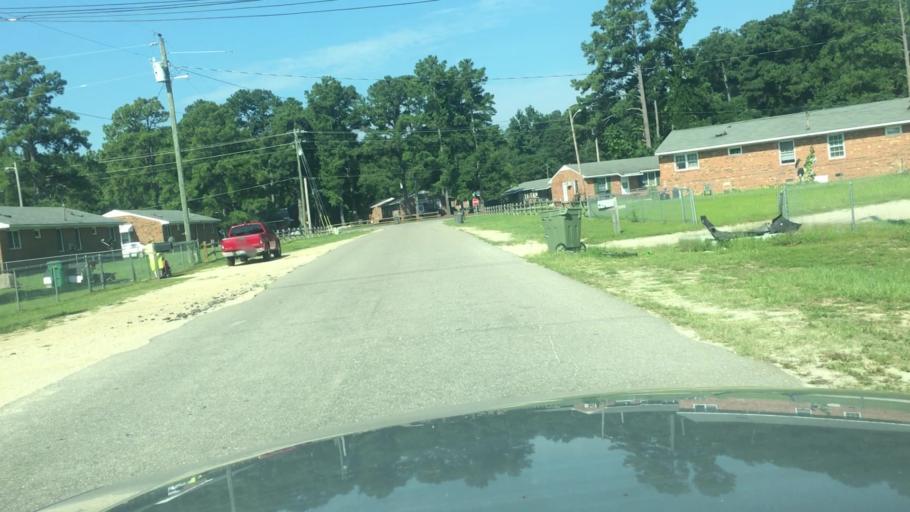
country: US
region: North Carolina
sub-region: Cumberland County
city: Spring Lake
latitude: 35.1446
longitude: -78.9124
